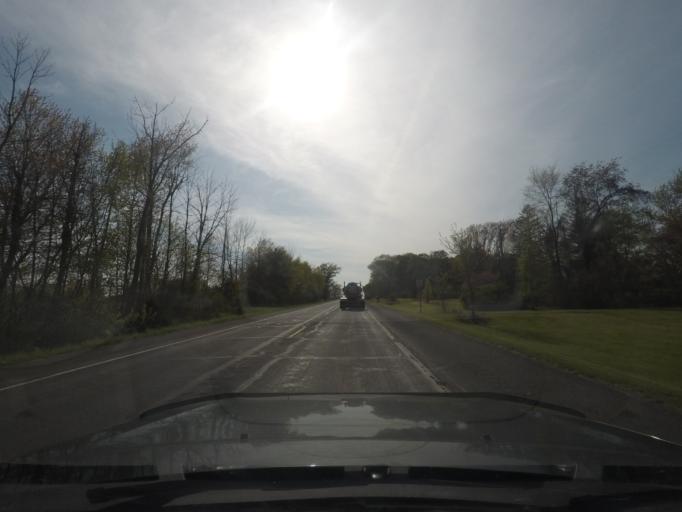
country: US
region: Indiana
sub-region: LaPorte County
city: Hudson Lake
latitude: 41.7980
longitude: -86.4866
